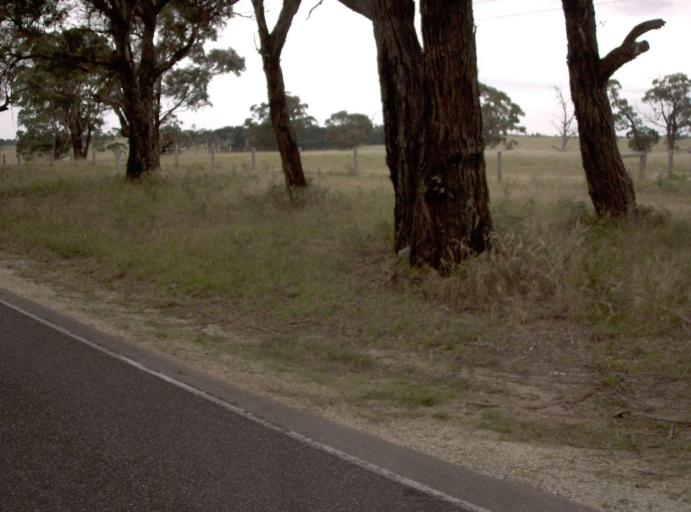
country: AU
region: Victoria
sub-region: Wellington
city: Sale
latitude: -38.1669
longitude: 147.1026
